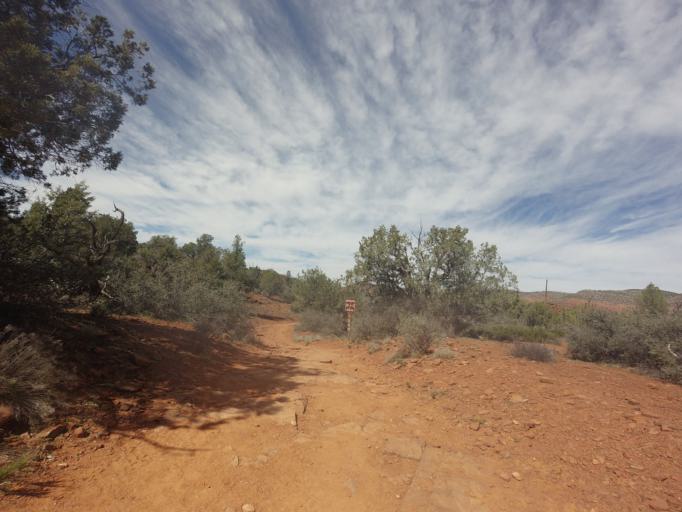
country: US
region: Arizona
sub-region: Yavapai County
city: West Sedona
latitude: 34.8090
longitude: -111.8217
